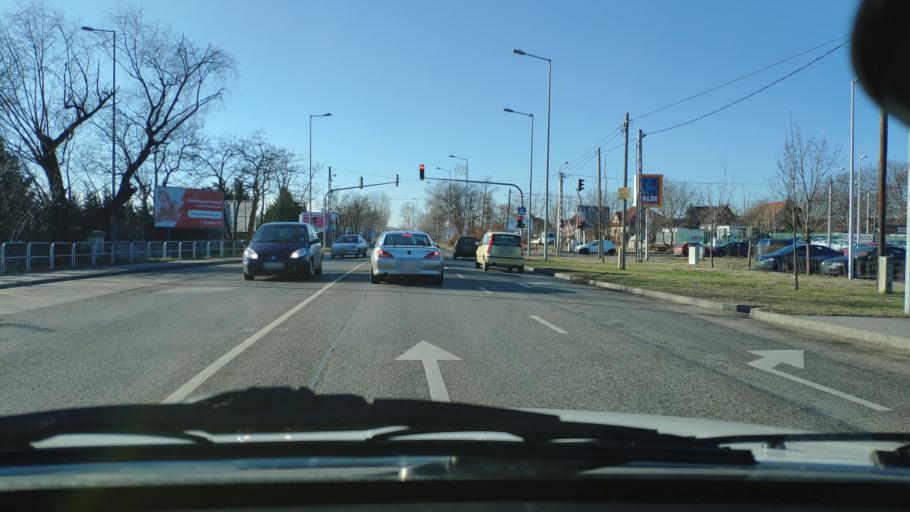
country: HU
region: Budapest
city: Budapest XXIII. keruelet
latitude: 47.4162
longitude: 19.1432
